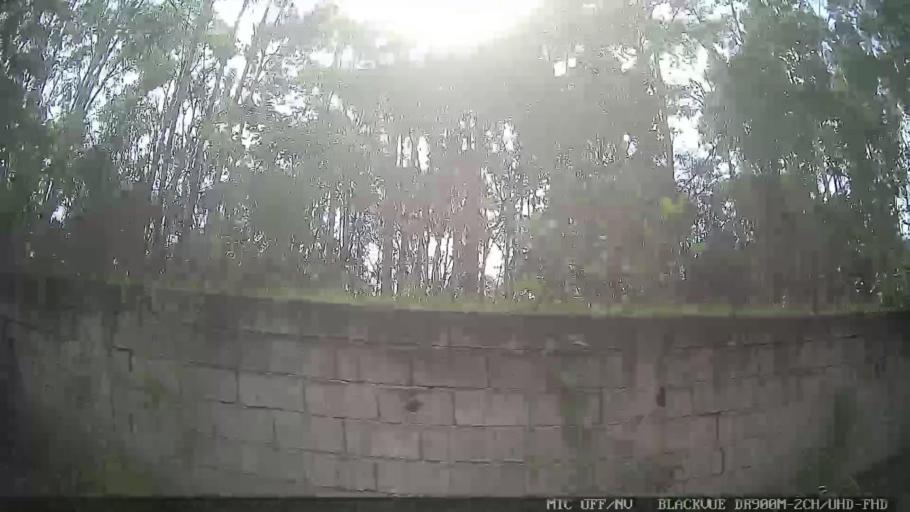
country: BR
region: Sao Paulo
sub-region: Jarinu
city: Jarinu
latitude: -23.0564
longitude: -46.6416
